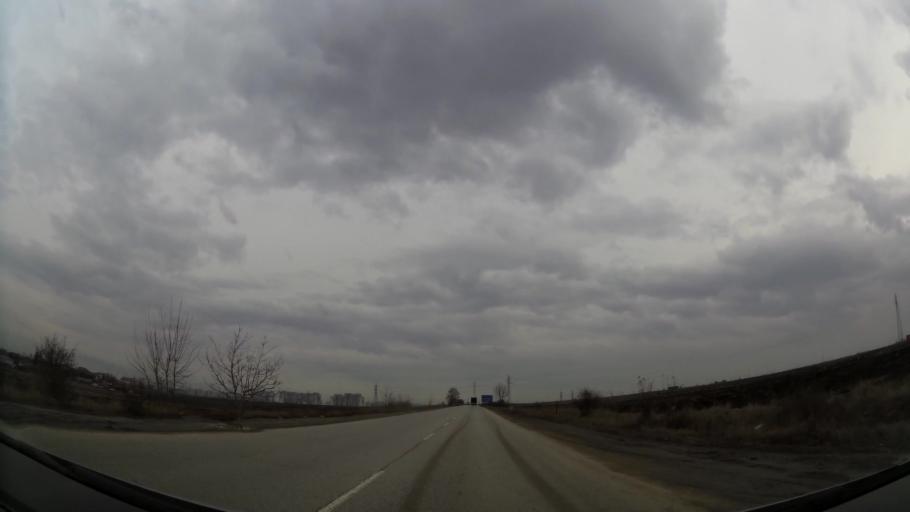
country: BG
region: Sofiya
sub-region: Obshtina Bozhurishte
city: Bozhurishte
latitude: 42.7140
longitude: 23.2225
